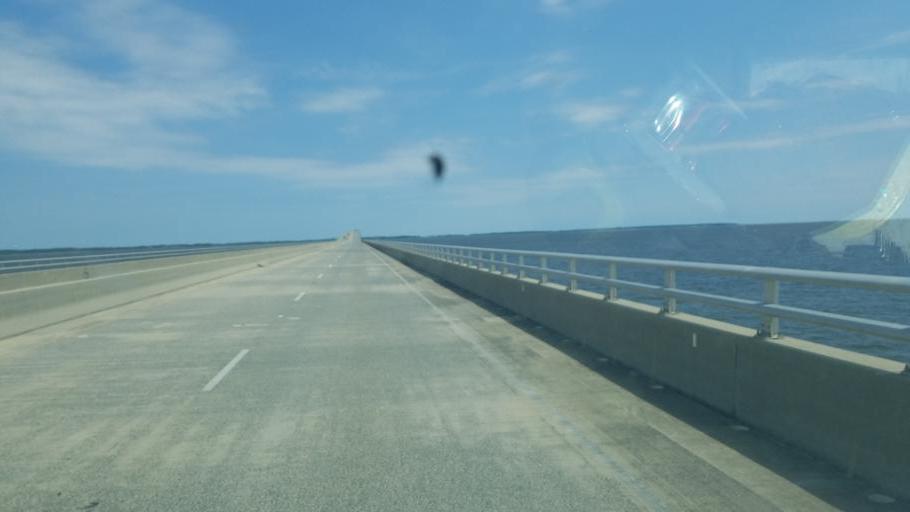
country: US
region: North Carolina
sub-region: Dare County
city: Manteo
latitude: 35.8869
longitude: -75.7323
